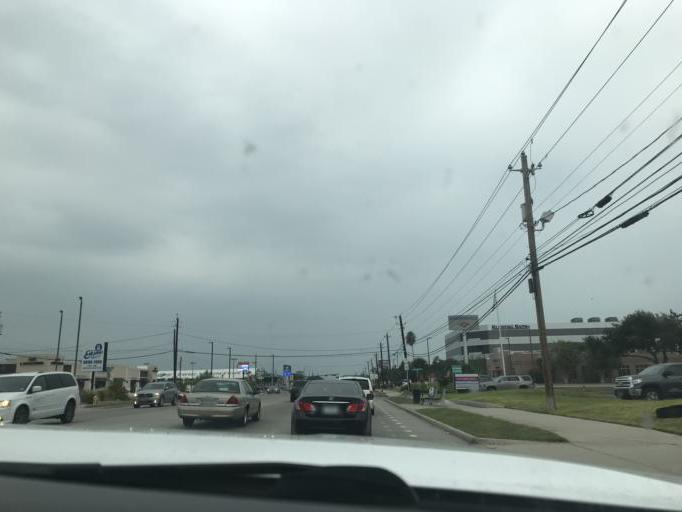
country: US
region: Texas
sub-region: Nueces County
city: Corpus Christi
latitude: 27.7024
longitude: -97.3732
